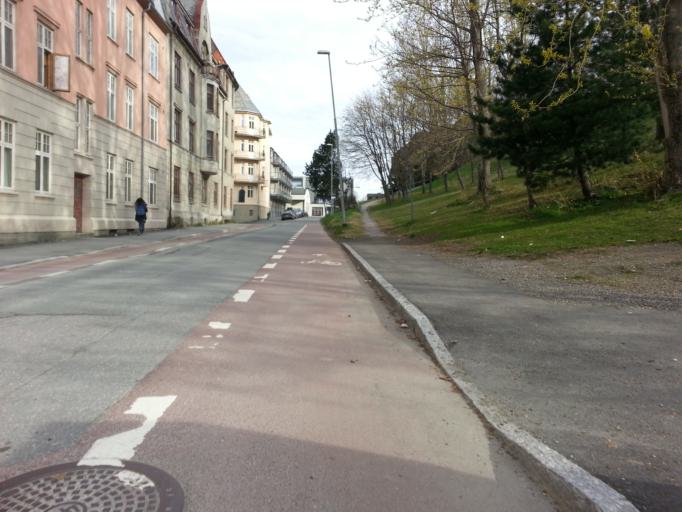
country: NO
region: Sor-Trondelag
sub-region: Trondheim
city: Trondheim
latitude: 63.4176
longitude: 10.3980
